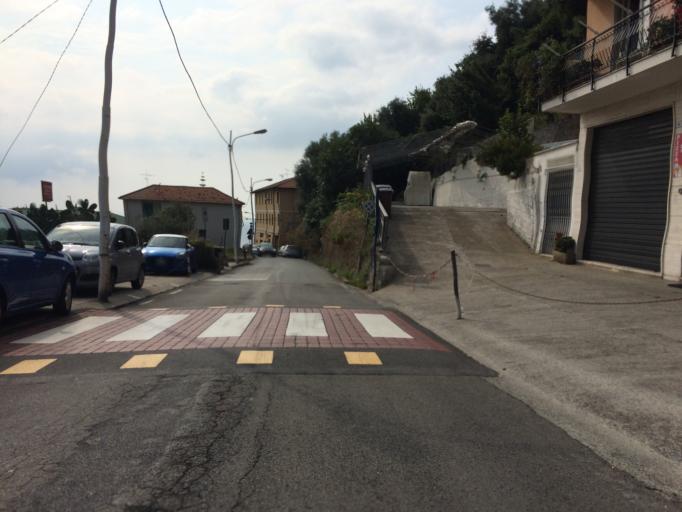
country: IT
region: Liguria
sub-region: Provincia di Imperia
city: San Remo
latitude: 43.8258
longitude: 7.7690
